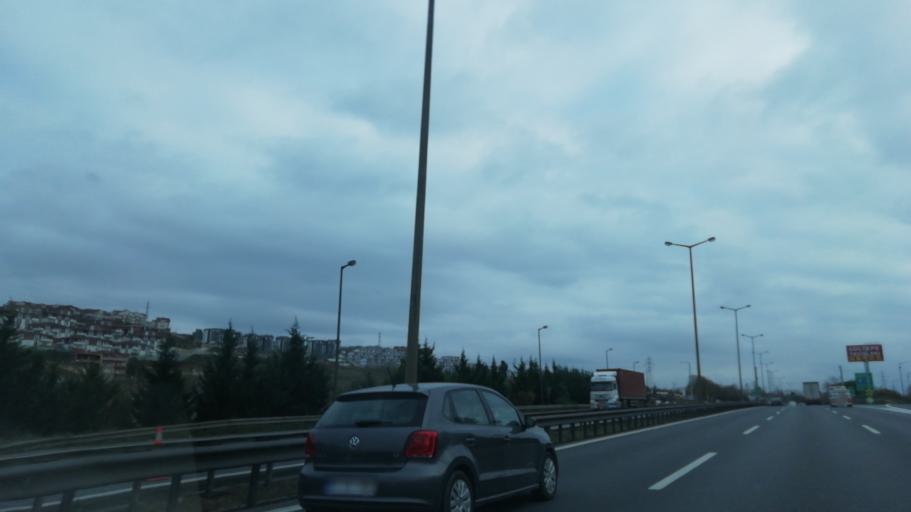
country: TR
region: Kocaeli
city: Izmit
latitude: 40.7804
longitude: 29.9241
